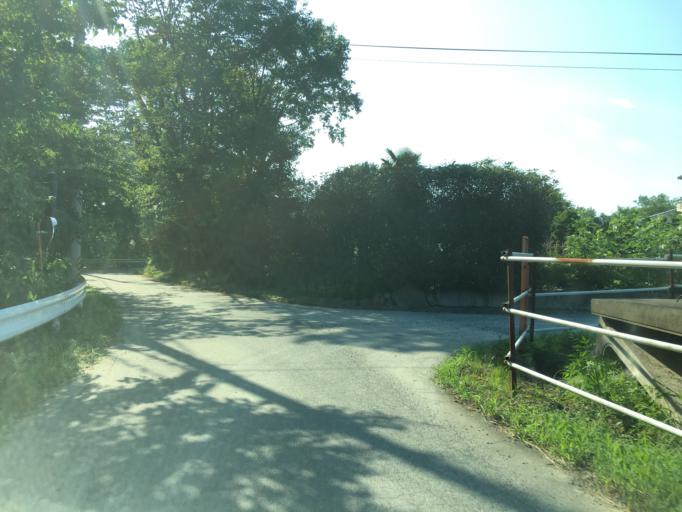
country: JP
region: Miyagi
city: Marumori
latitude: 37.8235
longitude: 140.8982
